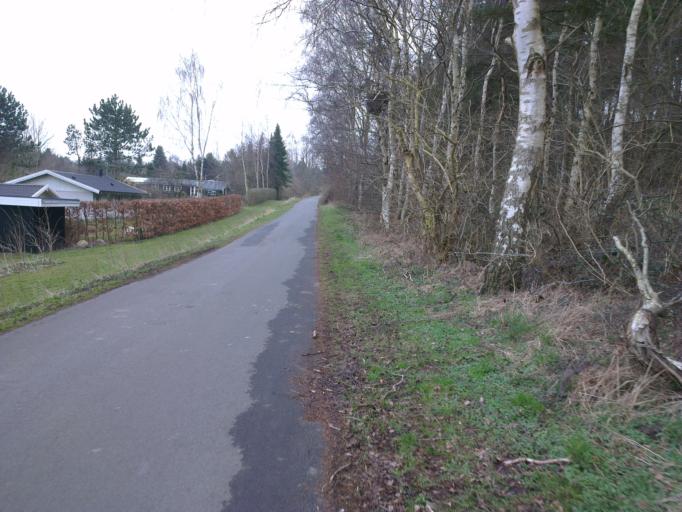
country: DK
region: Zealand
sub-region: Lejre Kommune
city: Ejby
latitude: 55.7406
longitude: 11.8679
